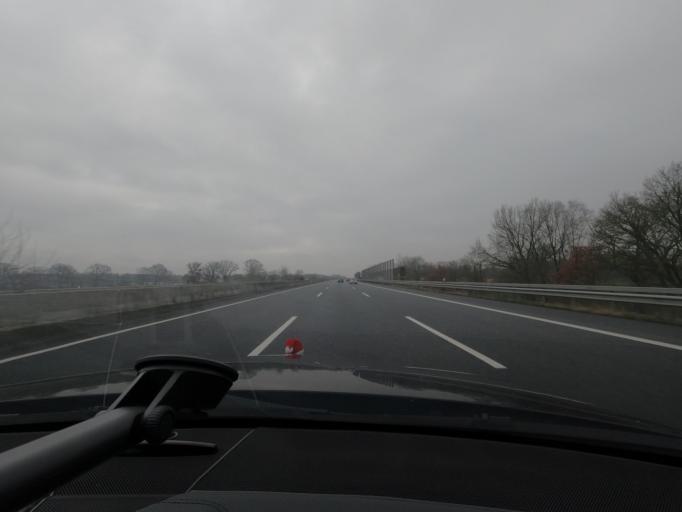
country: DE
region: Schleswig-Holstein
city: Ellerau
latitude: 53.7652
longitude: 9.9479
